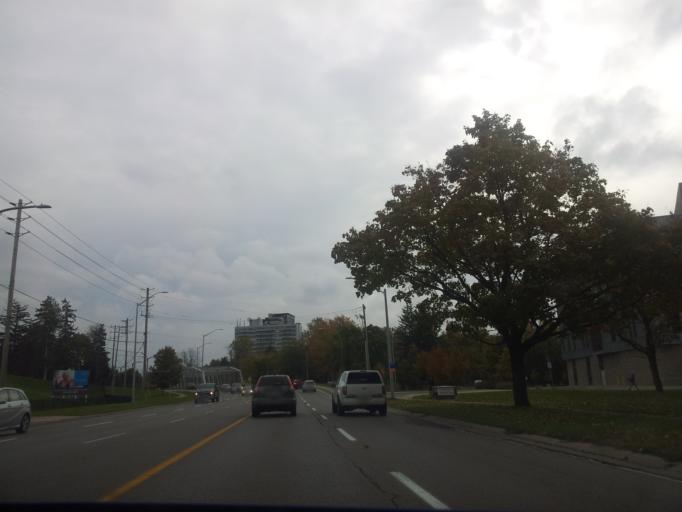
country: CA
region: Ontario
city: London
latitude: 43.0155
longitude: -81.2707
